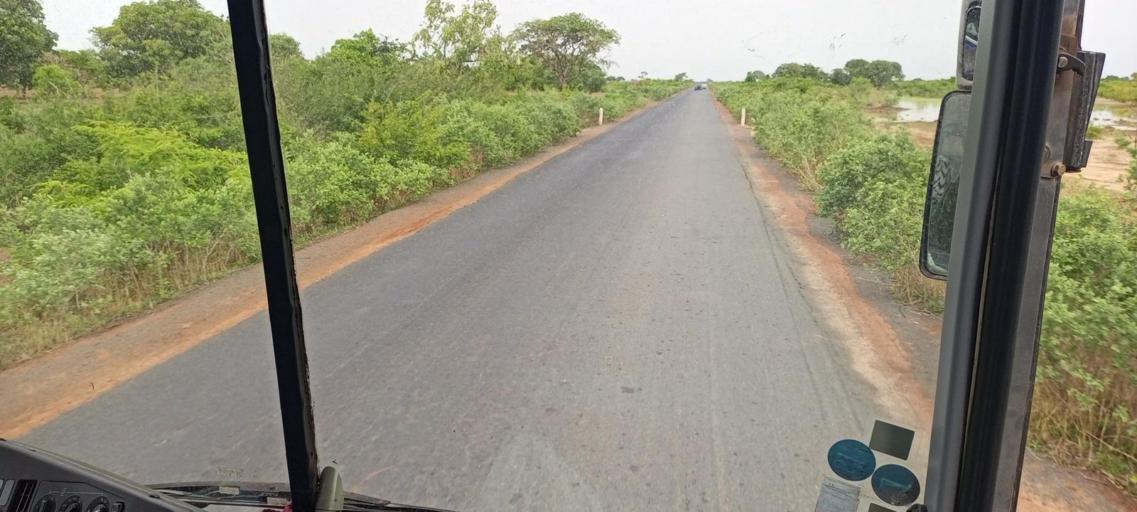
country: ML
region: Segou
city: Bla
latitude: 12.7620
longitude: -5.7388
